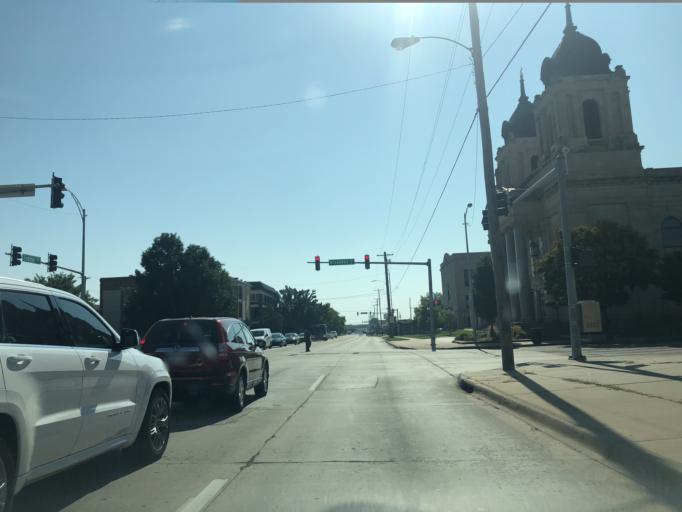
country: US
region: Kansas
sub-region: Sedgwick County
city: Wichita
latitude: 37.6934
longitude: -97.3355
